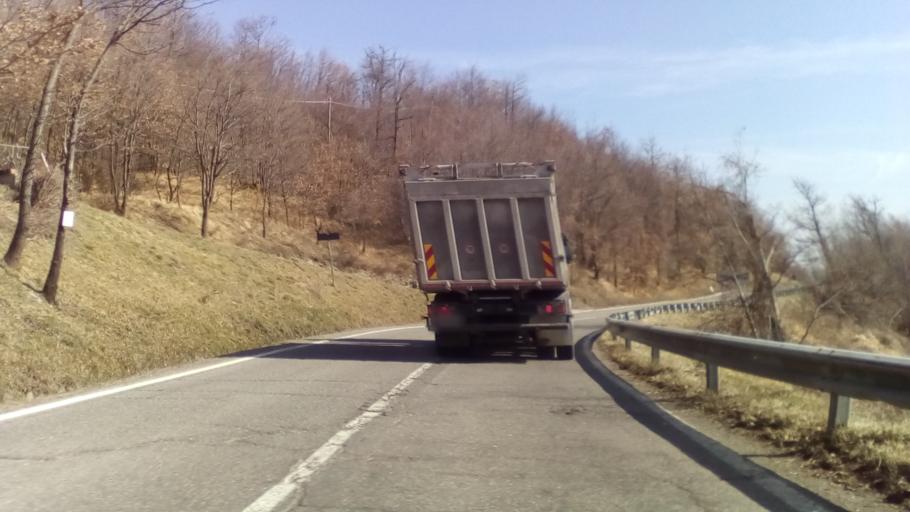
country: IT
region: Emilia-Romagna
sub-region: Provincia di Modena
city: Lama
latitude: 44.3108
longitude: 10.7428
